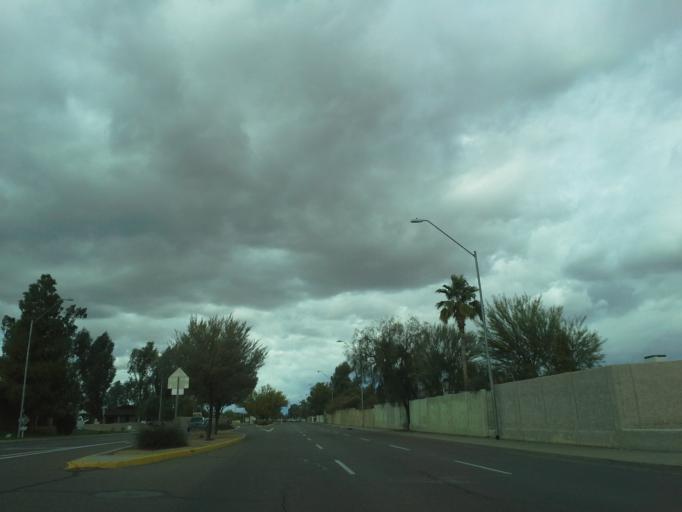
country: US
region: Arizona
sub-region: Maricopa County
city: Paradise Valley
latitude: 33.6195
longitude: -111.9778
